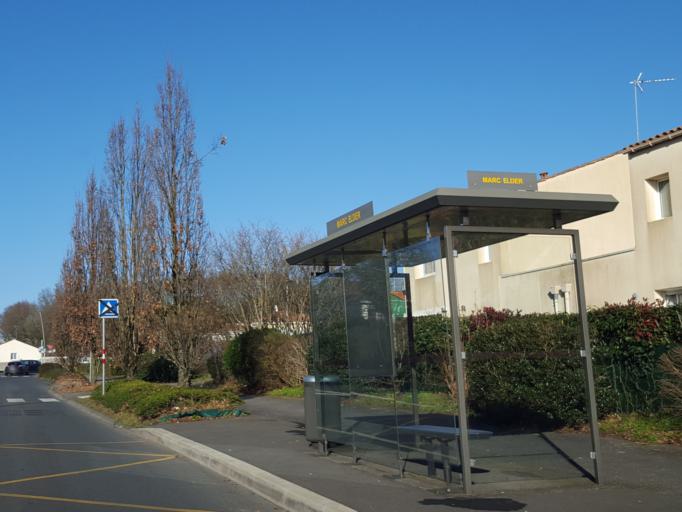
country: FR
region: Pays de la Loire
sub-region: Departement de la Vendee
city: La Roche-sur-Yon
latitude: 46.6629
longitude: -1.4541
